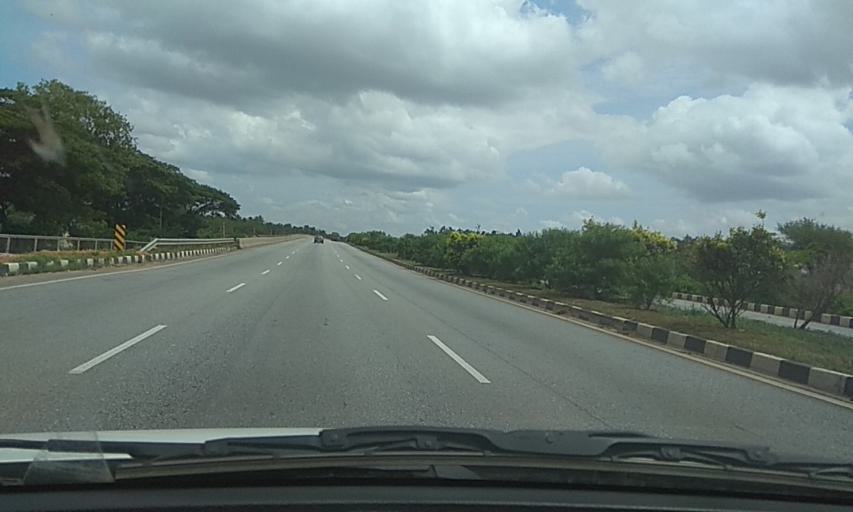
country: IN
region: Karnataka
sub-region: Tumkur
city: Tumkur
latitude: 13.4147
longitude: 77.0820
